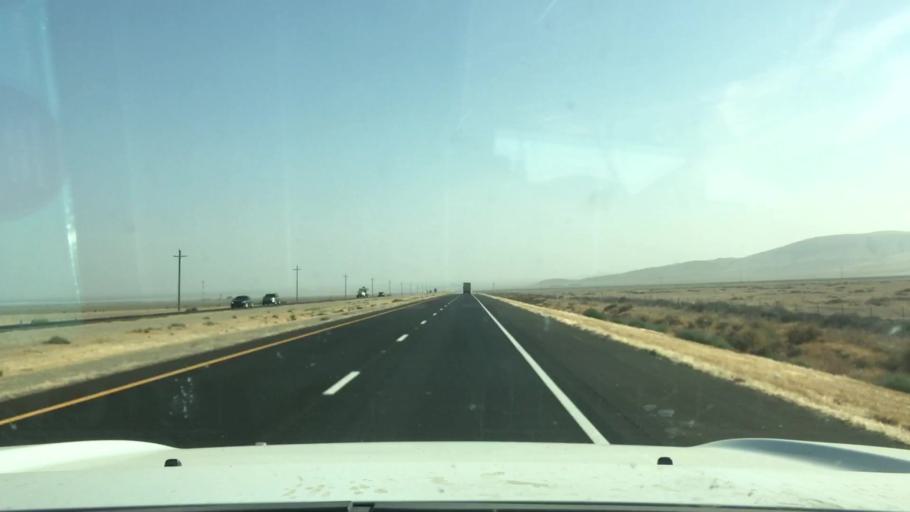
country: US
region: California
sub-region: San Luis Obispo County
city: Shandon
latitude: 35.6638
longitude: -120.0672
